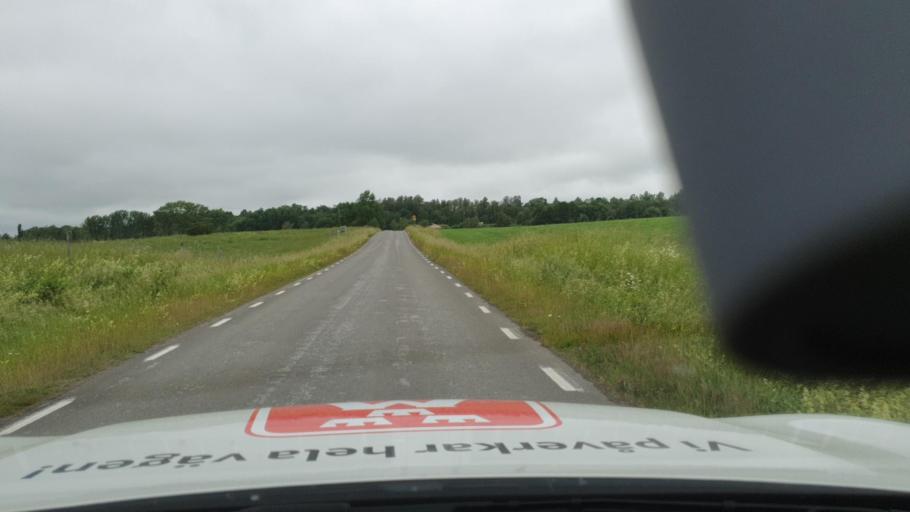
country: SE
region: Vaestra Goetaland
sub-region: Skovde Kommun
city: Stopen
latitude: 58.3939
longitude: 13.9878
